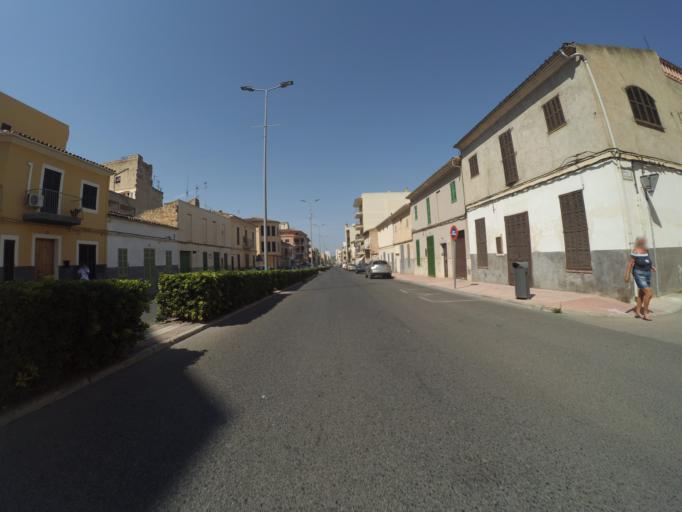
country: ES
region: Balearic Islands
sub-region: Illes Balears
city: Manacor
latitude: 39.5636
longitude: 3.2077
